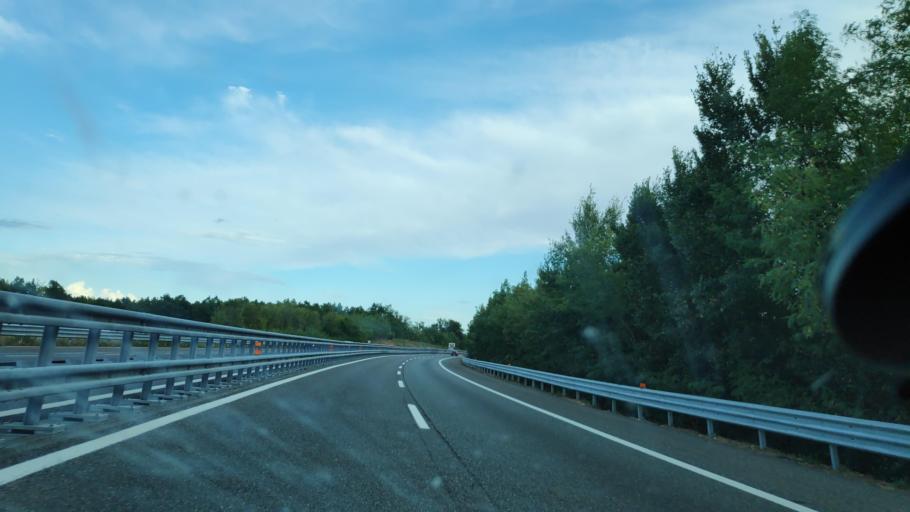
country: IT
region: Piedmont
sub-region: Provincia di Asti
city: Refrancore
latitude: 44.9101
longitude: 8.3297
